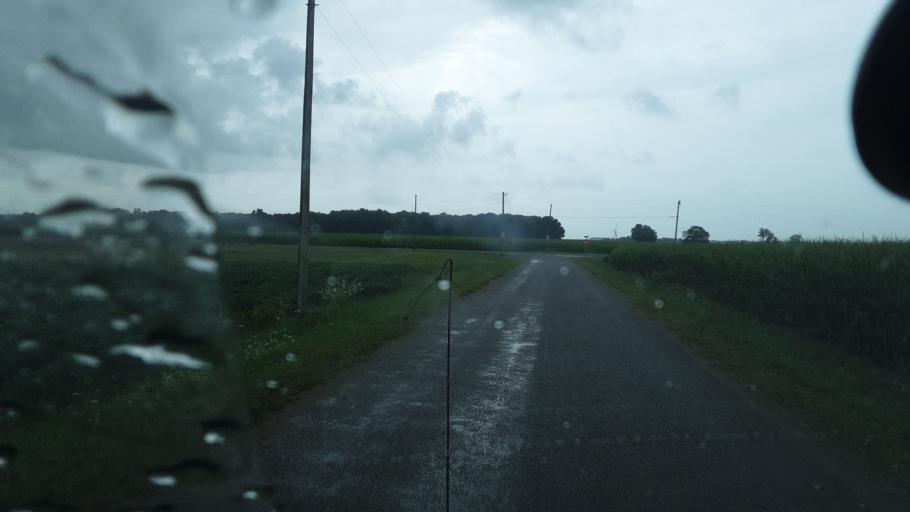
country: US
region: Indiana
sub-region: Steuben County
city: Hamilton
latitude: 41.5373
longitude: -84.8174
